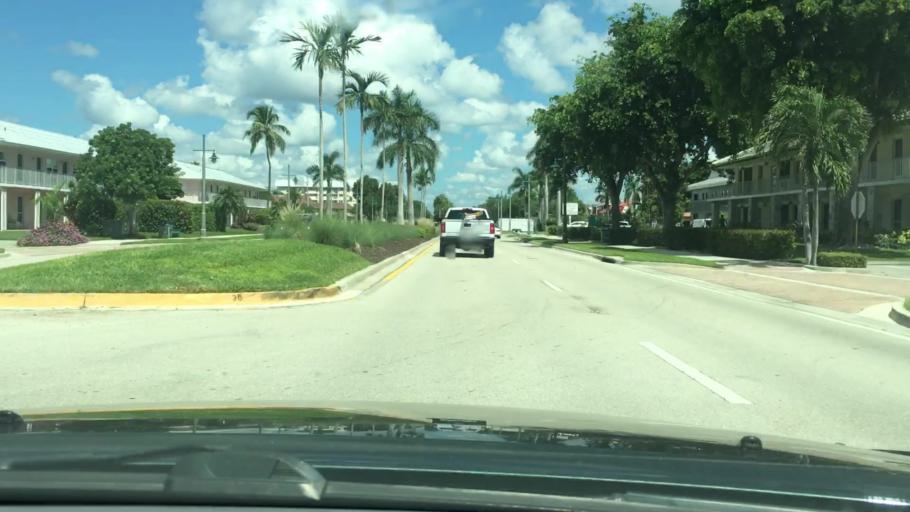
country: US
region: Florida
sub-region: Collier County
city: Marco
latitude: 25.9407
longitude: -81.7326
